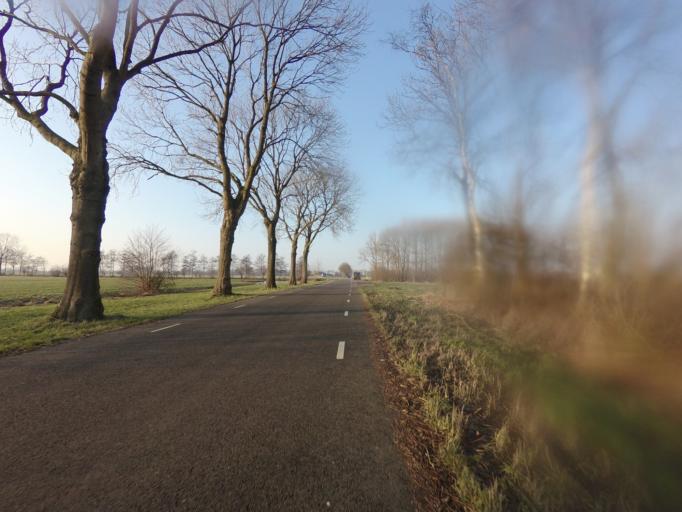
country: NL
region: South Holland
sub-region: Gemeente Vlist
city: Vlist
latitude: 52.0068
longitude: 4.8112
